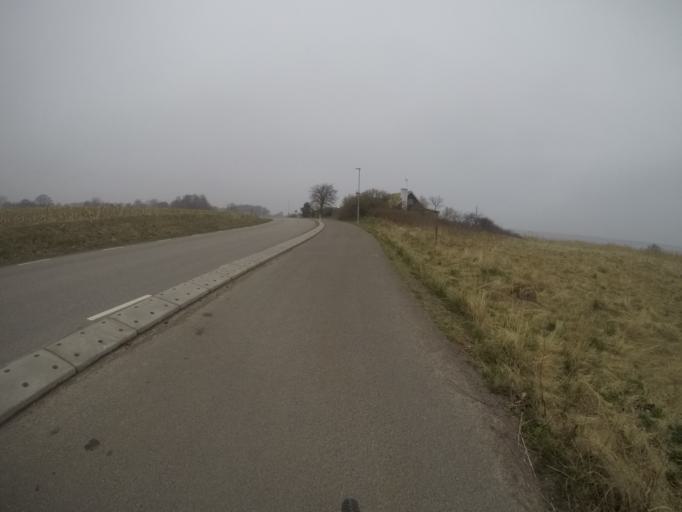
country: SE
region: Skane
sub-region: Angelholms Kommun
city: Strovelstorp
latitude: 56.2181
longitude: 12.7690
